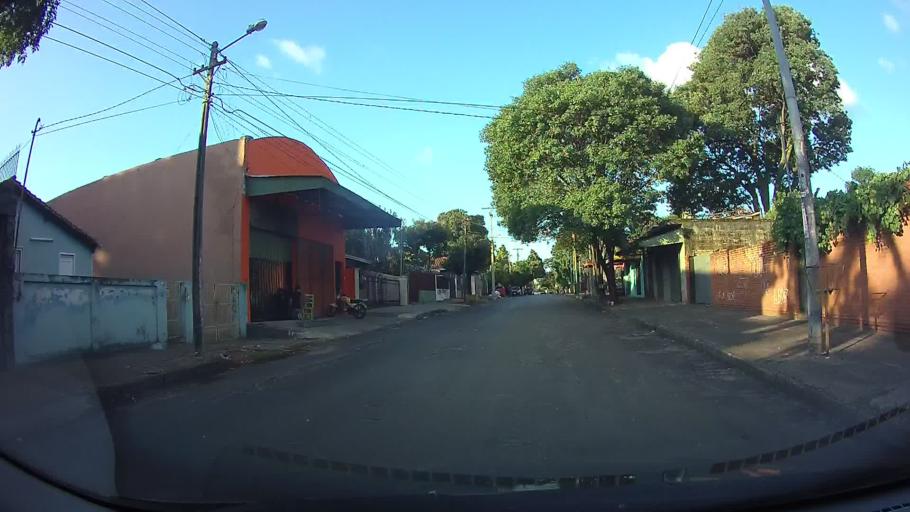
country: PY
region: Central
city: Lambare
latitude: -25.3226
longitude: -57.5728
